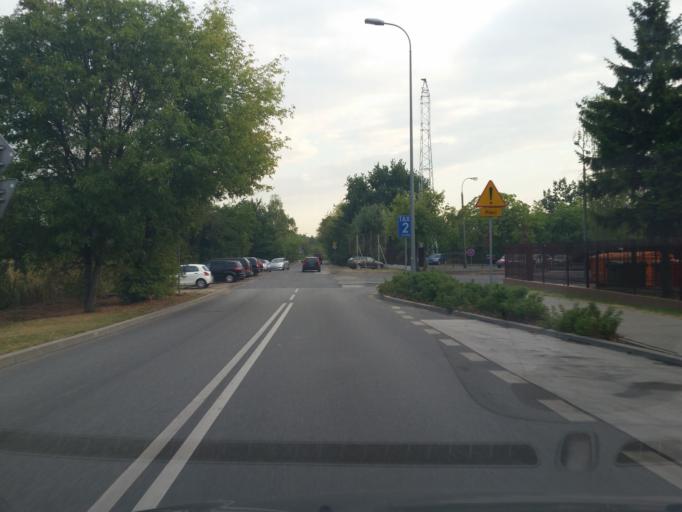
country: PL
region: Masovian Voivodeship
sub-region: Warszawa
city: Wlochy
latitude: 52.1770
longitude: 20.9837
